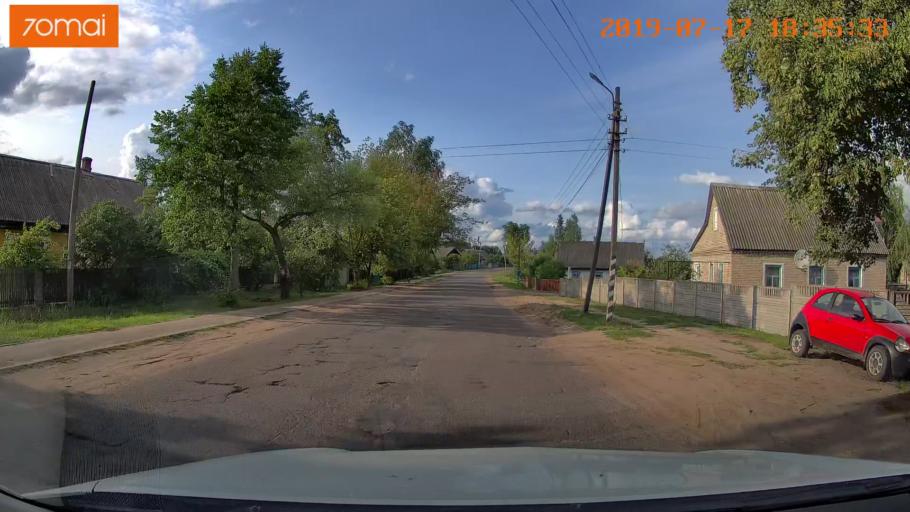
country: BY
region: Mogilev
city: Asipovichy
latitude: 53.2930
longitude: 28.6585
